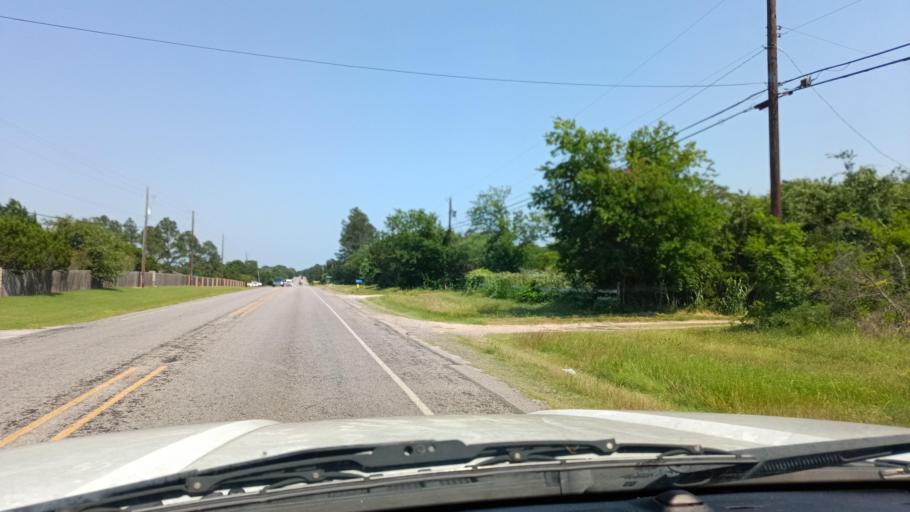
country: US
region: Texas
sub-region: Bell County
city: Morgans Point Resort
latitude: 31.1044
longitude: -97.5017
